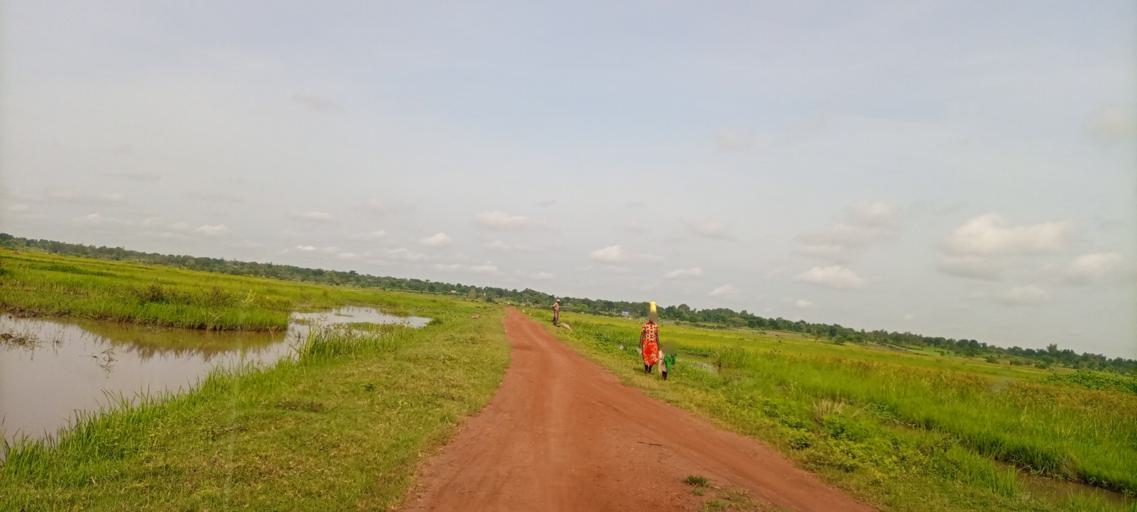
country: UG
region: Eastern Region
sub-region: Kibuku District
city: Kibuku
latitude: 1.1008
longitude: 33.7761
